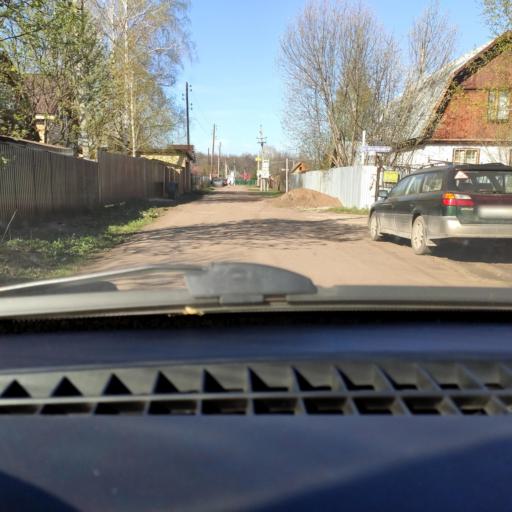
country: RU
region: Bashkortostan
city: Ufa
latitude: 54.6882
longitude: 55.9016
